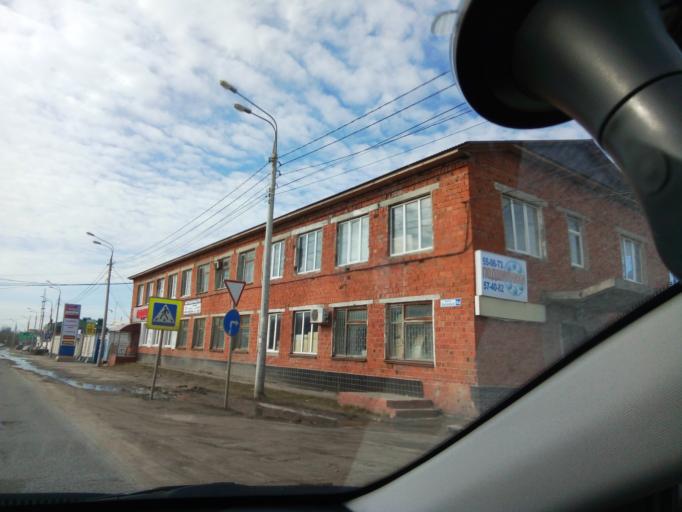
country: RU
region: Chuvashia
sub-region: Cheboksarskiy Rayon
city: Cheboksary
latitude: 56.1060
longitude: 47.2490
